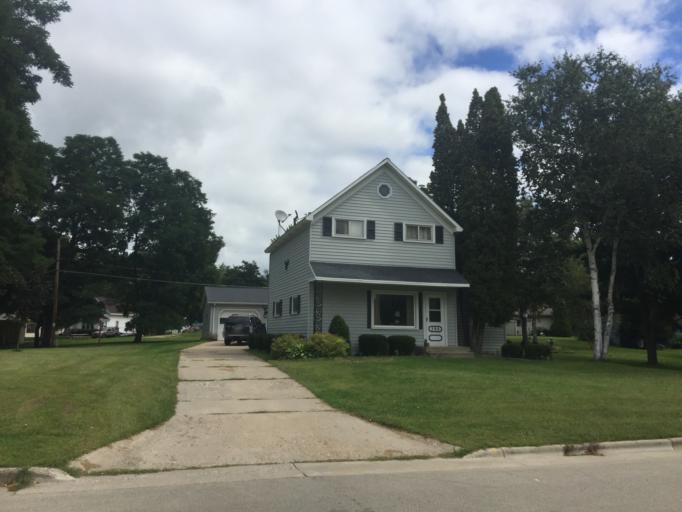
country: US
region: Wisconsin
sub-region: Oconto County
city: Oconto Falls
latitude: 44.8712
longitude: -88.1373
